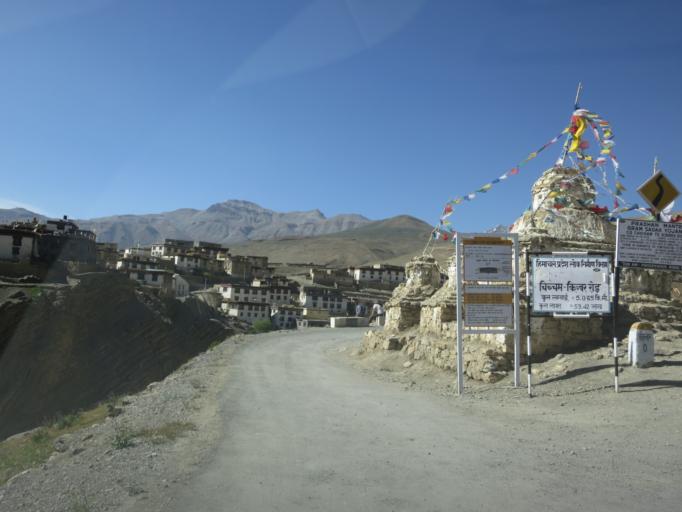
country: IN
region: Himachal Pradesh
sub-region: Kulu
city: Manali
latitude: 32.3297
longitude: 78.0081
